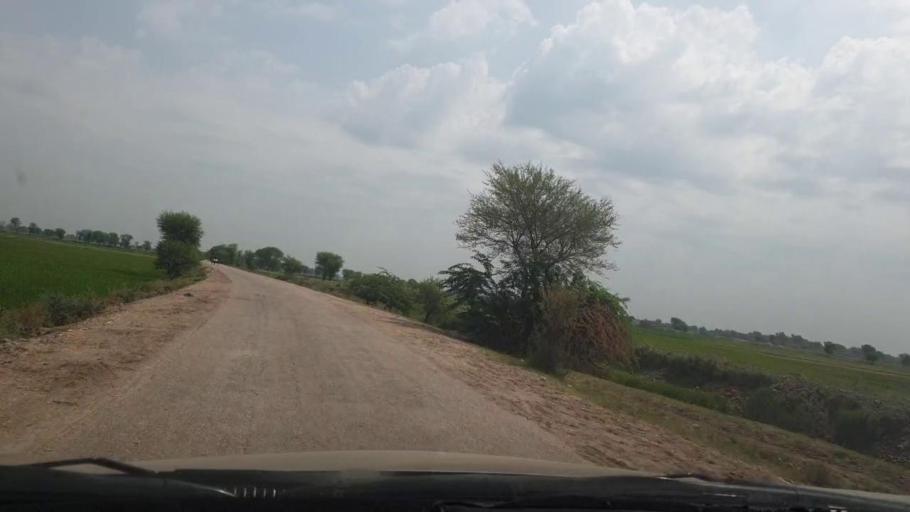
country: PK
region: Sindh
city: Miro Khan
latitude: 27.6828
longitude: 68.1877
